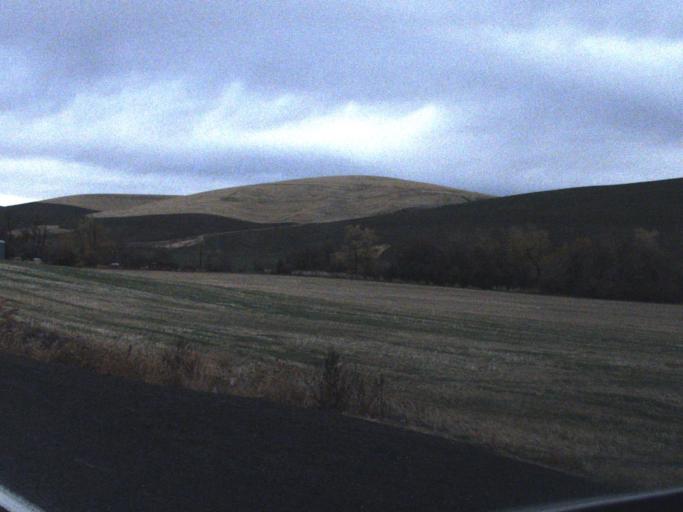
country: US
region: Washington
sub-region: Walla Walla County
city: Waitsburg
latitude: 46.2347
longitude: -118.1392
